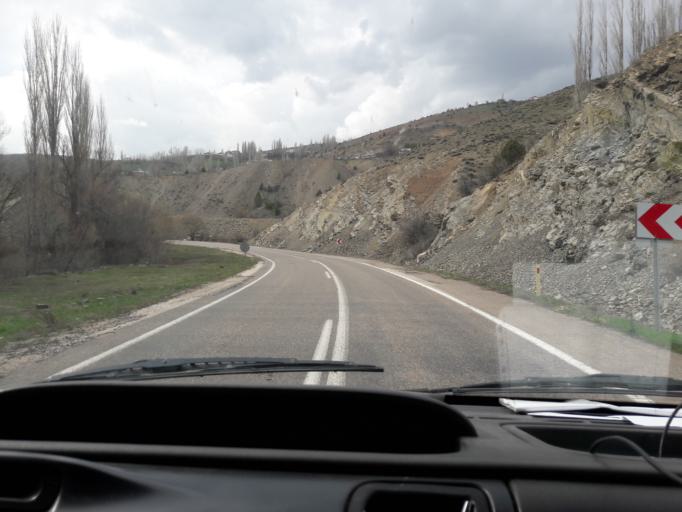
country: TR
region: Giresun
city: Alucra
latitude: 40.2706
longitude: 38.8835
